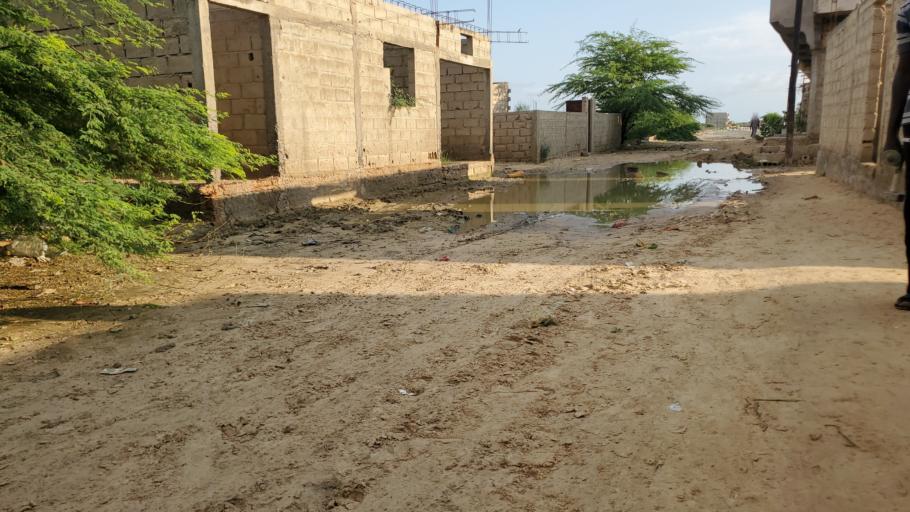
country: SN
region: Saint-Louis
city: Saint-Louis
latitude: 16.0592
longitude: -16.4188
